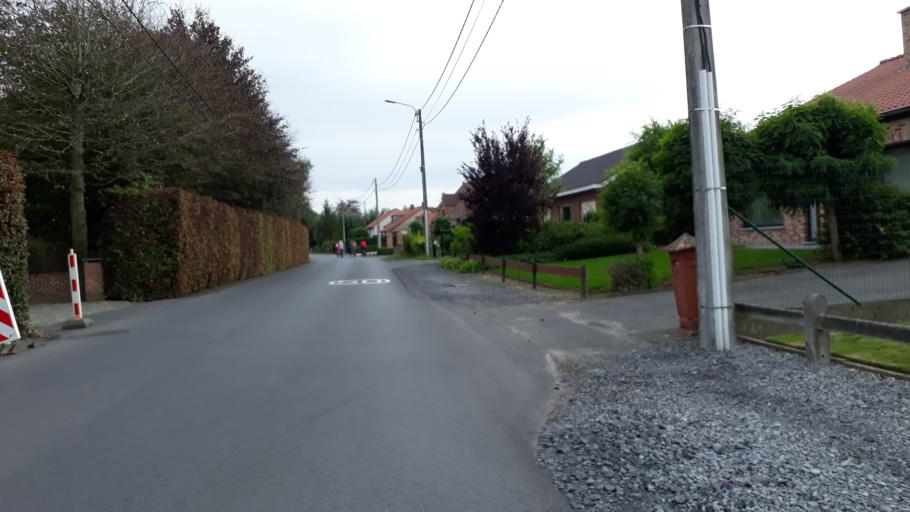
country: BE
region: Flanders
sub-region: Provincie West-Vlaanderen
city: Lichtervelde
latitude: 51.0355
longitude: 3.1166
